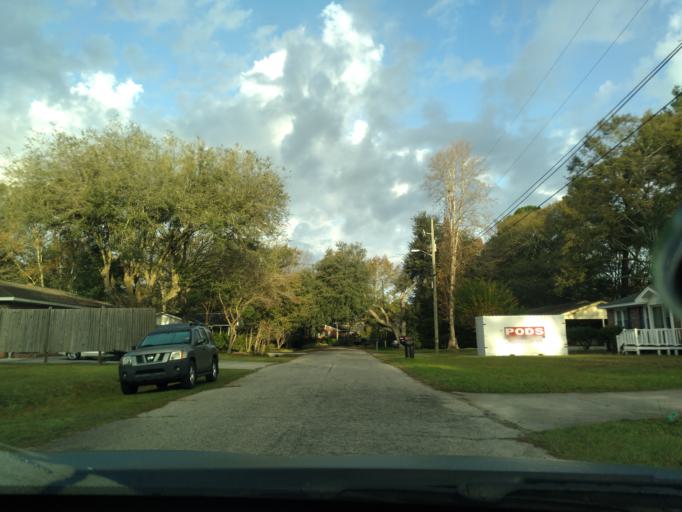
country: US
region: South Carolina
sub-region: Charleston County
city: North Charleston
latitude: 32.8060
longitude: -80.0063
